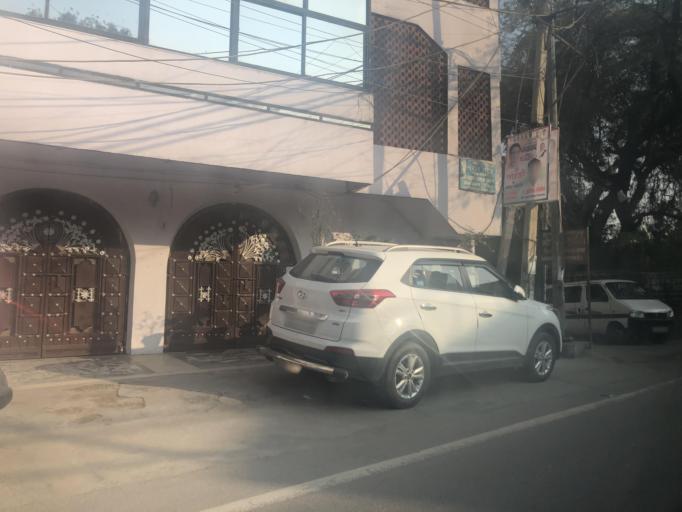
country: IN
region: Haryana
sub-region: Gurgaon
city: Gurgaon
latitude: 28.5641
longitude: 77.0010
